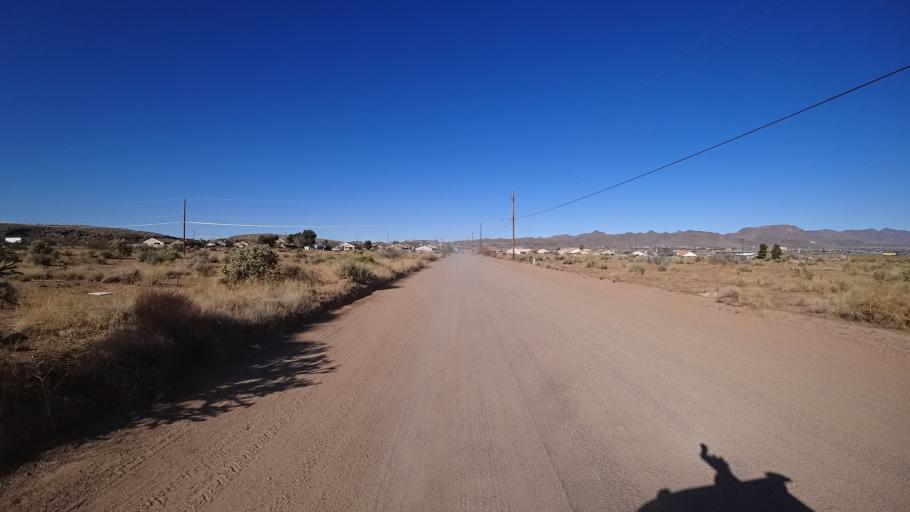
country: US
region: Arizona
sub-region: Mohave County
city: Kingman
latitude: 35.2121
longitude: -114.0004
